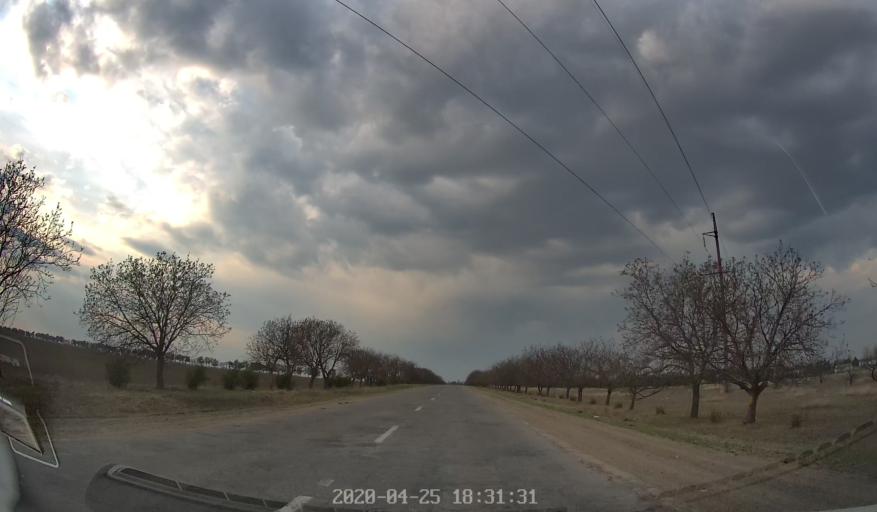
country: MD
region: Criuleni
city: Criuleni
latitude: 47.2184
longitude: 29.1469
